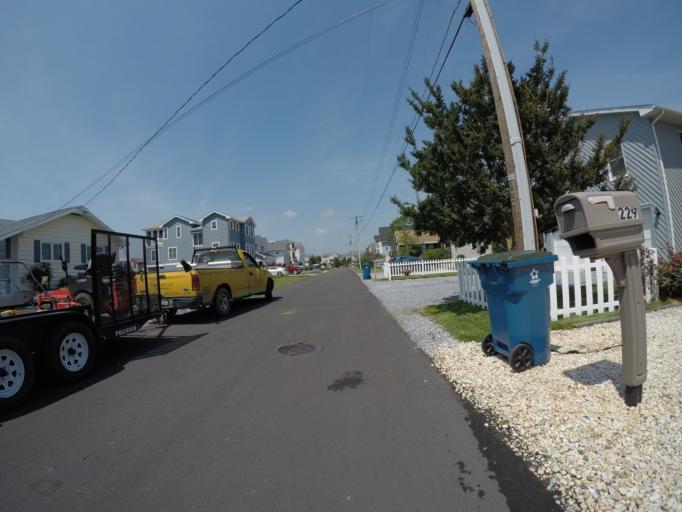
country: US
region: Delaware
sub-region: Sussex County
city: Bethany Beach
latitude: 38.5145
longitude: -75.0593
